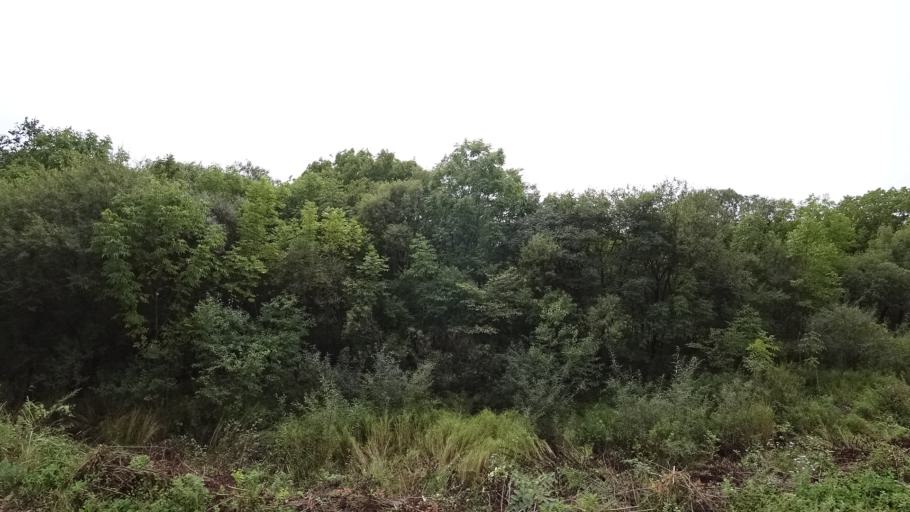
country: RU
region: Primorskiy
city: Lyalichi
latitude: 44.0819
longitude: 132.4489
